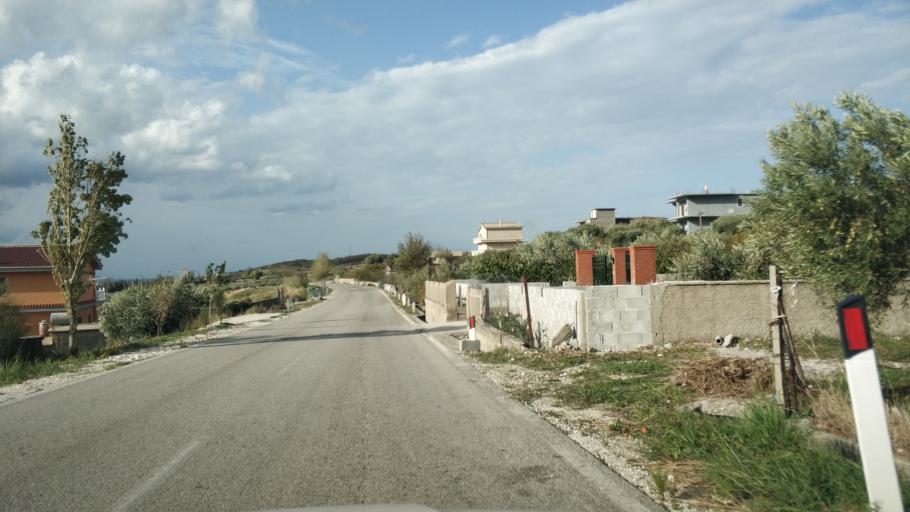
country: AL
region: Vlore
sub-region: Rrethi i Vlores
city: Orikum
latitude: 40.3086
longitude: 19.4817
